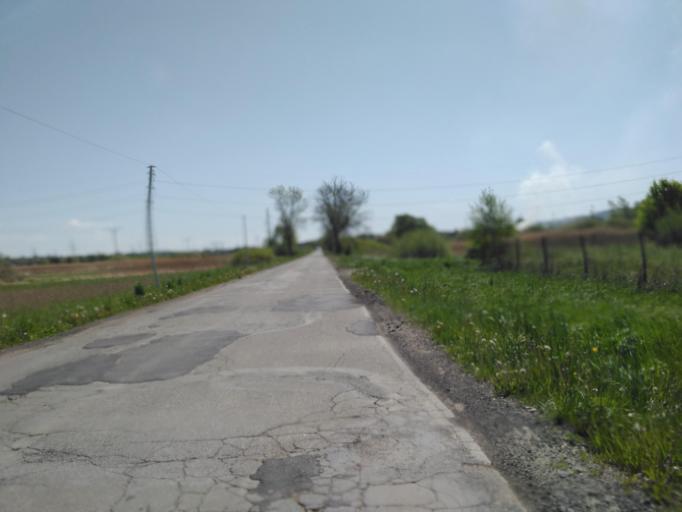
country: PL
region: Subcarpathian Voivodeship
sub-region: Powiat krosnienski
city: Miejsce Piastowe
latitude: 49.6080
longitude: 21.7750
